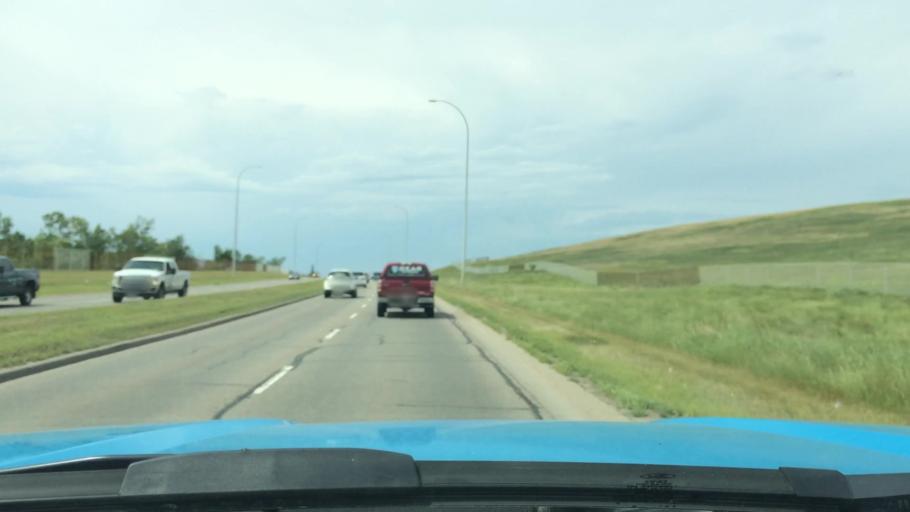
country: CA
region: Alberta
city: Calgary
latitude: 51.0985
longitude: -114.1188
